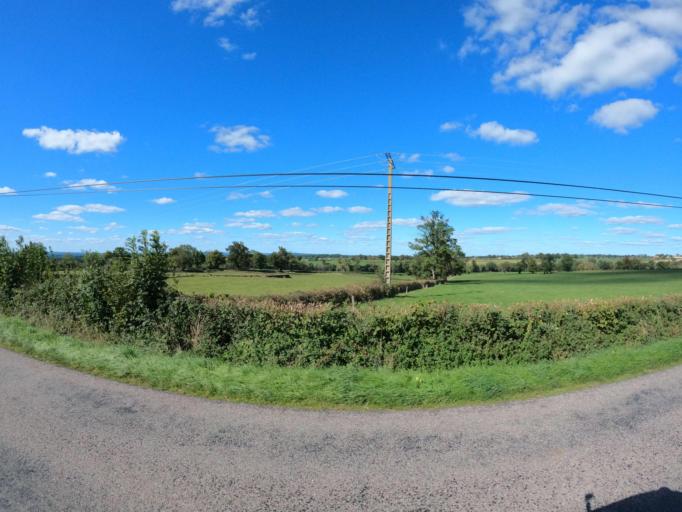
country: FR
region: Auvergne
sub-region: Departement de l'Allier
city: Buxieres-les-Mines
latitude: 46.4041
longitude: 2.9285
